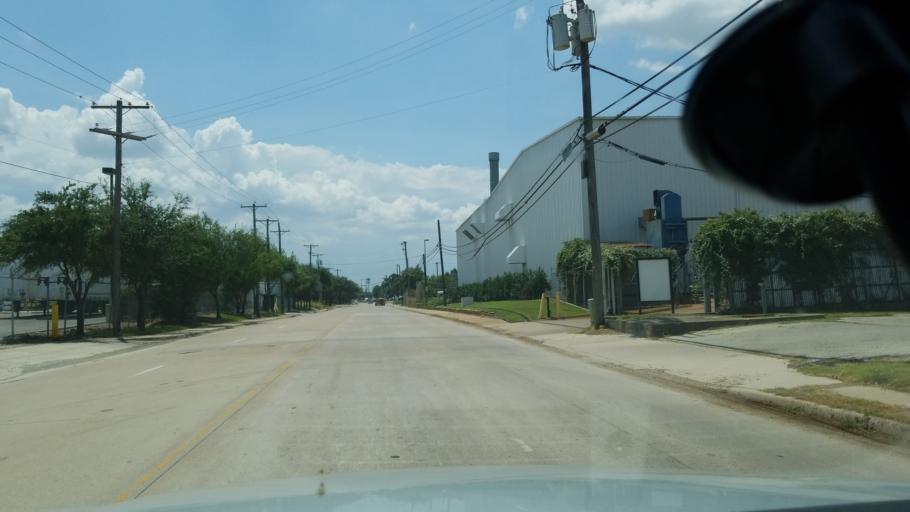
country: US
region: Texas
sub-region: Dallas County
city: Farmers Branch
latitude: 32.8721
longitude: -96.9078
